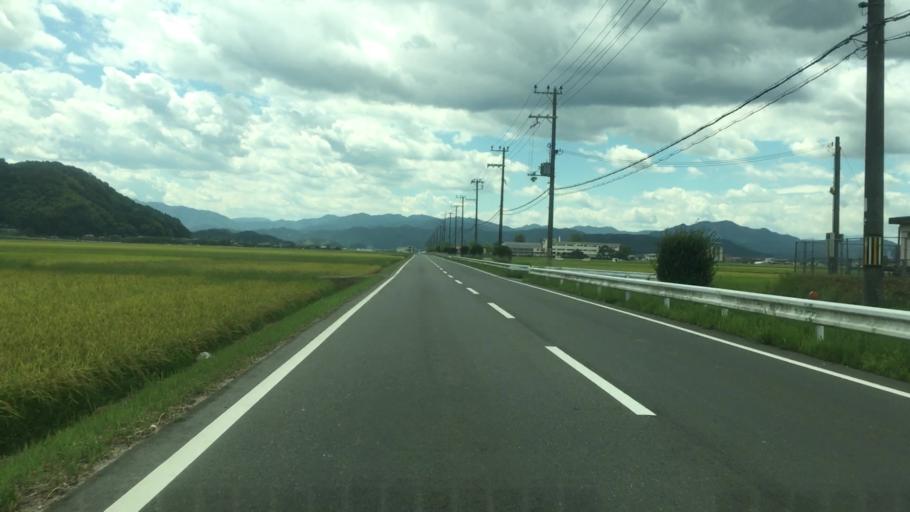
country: JP
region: Hyogo
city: Toyooka
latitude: 35.5375
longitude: 134.8397
